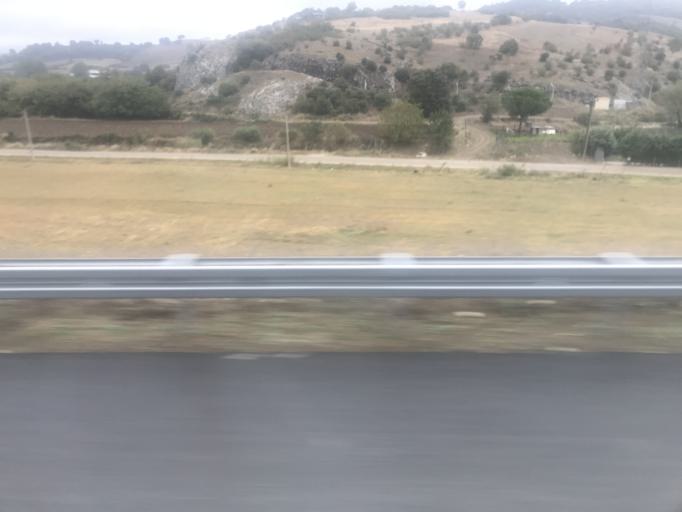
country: TR
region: Balikesir
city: Susurluk
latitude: 39.9175
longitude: 28.1289
